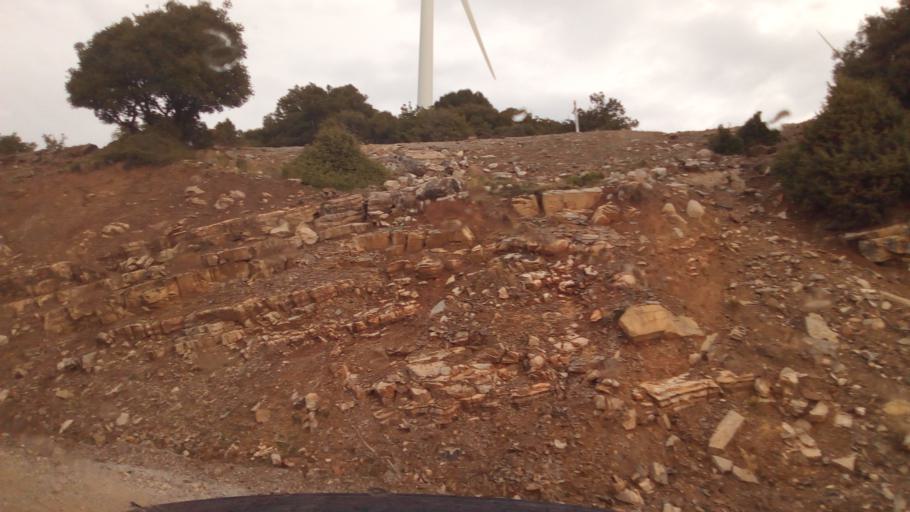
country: GR
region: West Greece
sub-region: Nomos Achaias
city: Kamarai
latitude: 38.4263
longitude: 22.0428
